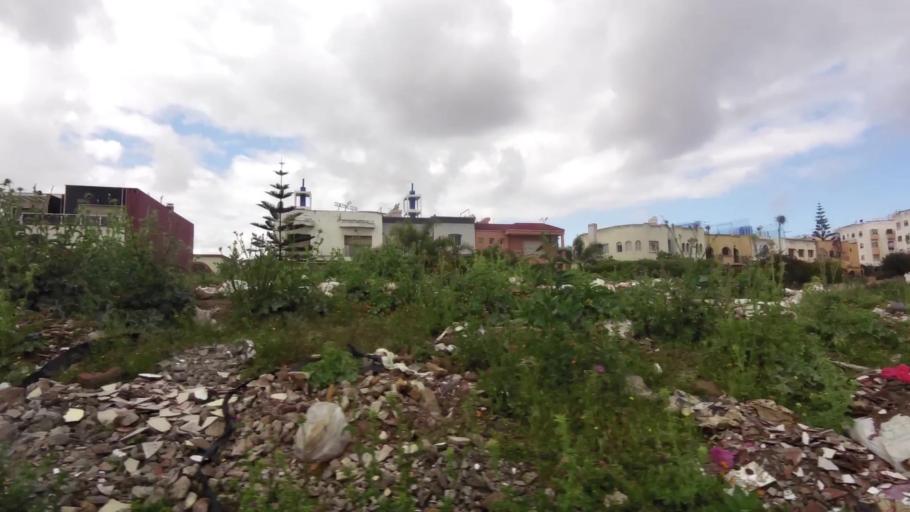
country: MA
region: Grand Casablanca
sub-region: Nouaceur
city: Bouskoura
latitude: 33.5196
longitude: -7.6439
